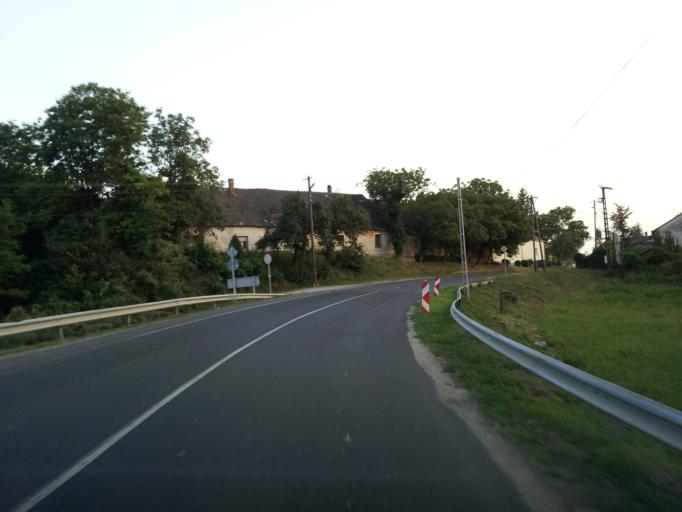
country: HU
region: Veszprem
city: Revfueloep
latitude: 46.9269
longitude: 17.5595
